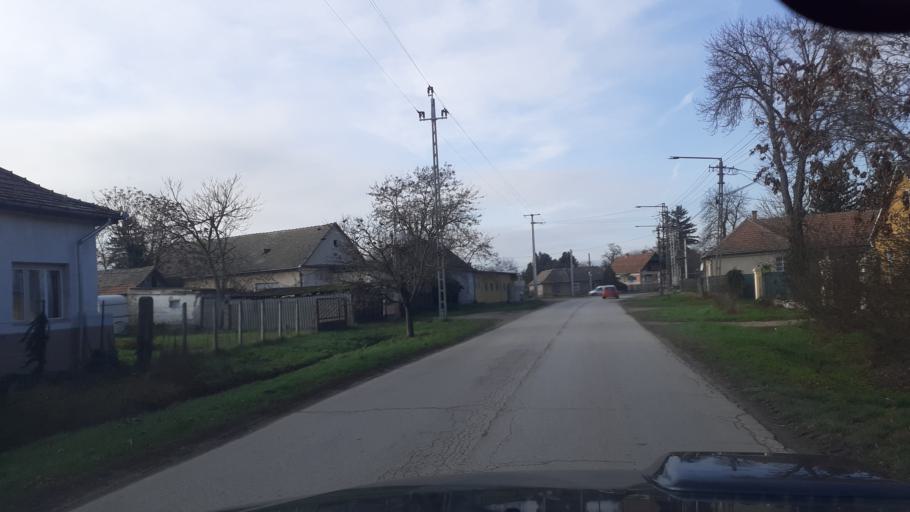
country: HU
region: Pest
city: Domsod
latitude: 47.0939
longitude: 19.0105
